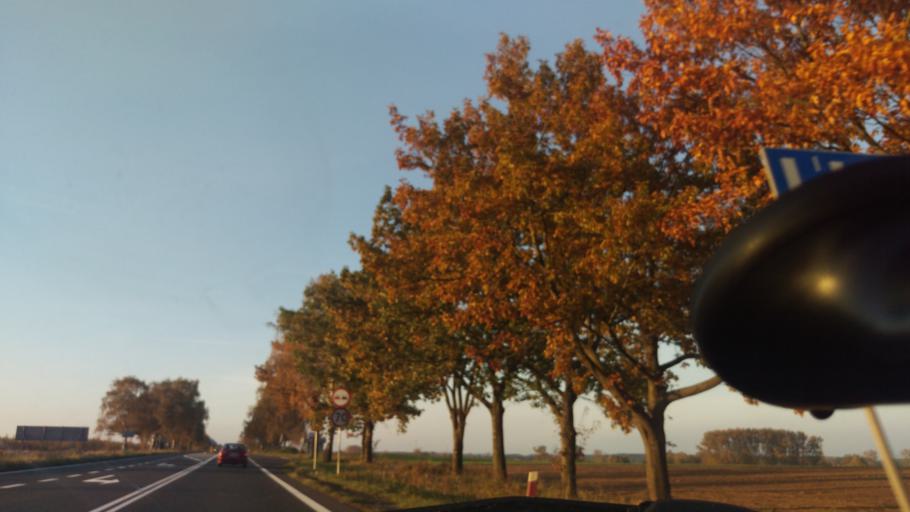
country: PL
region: West Pomeranian Voivodeship
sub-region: Powiat gryfinski
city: Stare Czarnowo
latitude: 53.2301
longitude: 14.7925
